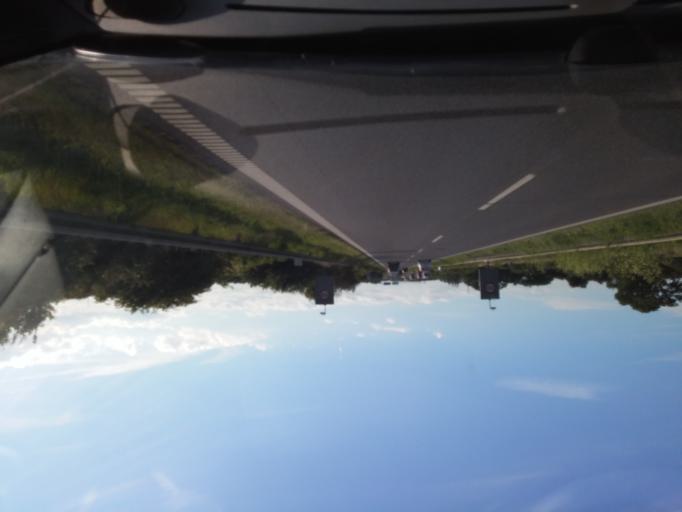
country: DK
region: Zealand
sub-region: Slagelse Kommune
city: Korsor
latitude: 55.3554
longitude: 11.1524
